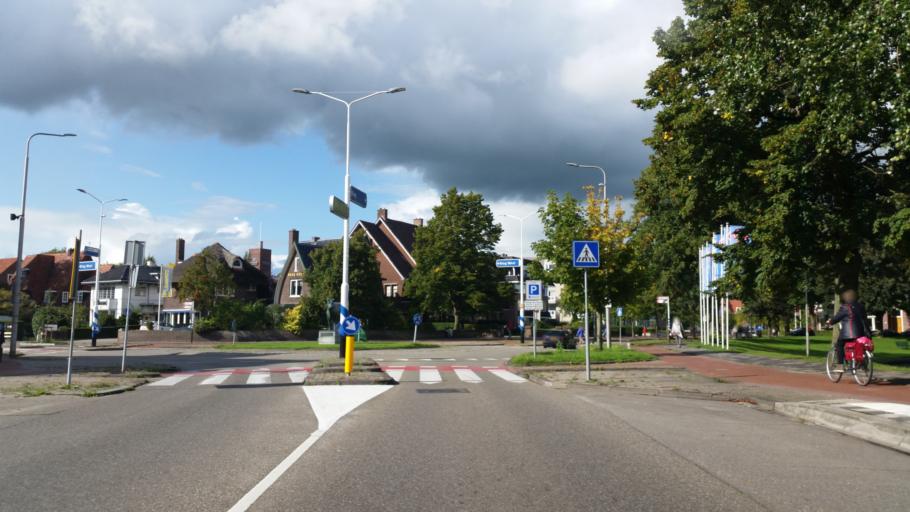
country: NL
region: Friesland
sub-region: Gemeente Leeuwarden
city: Bilgaard
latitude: 53.2037
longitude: 5.7876
